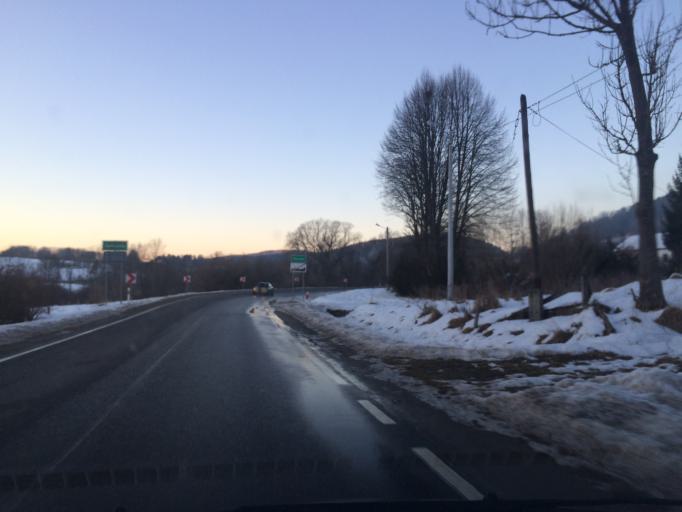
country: PL
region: Subcarpathian Voivodeship
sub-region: Powiat bieszczadzki
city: Czarna
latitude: 49.3790
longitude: 22.6421
